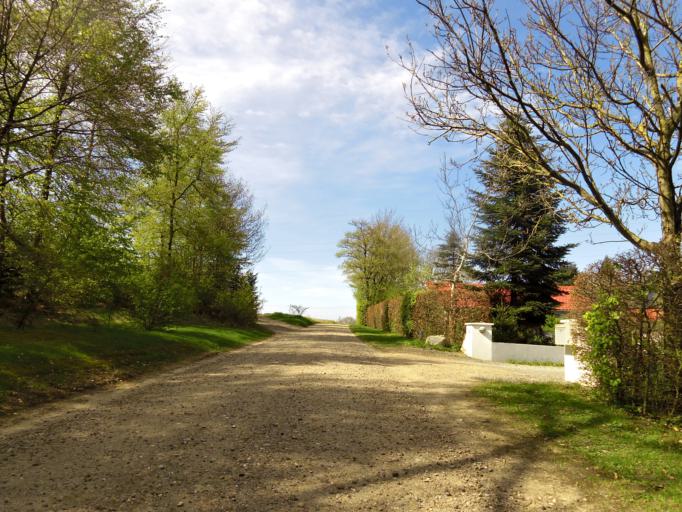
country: DK
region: Central Jutland
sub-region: Holstebro Kommune
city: Vinderup
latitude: 56.4653
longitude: 8.8907
